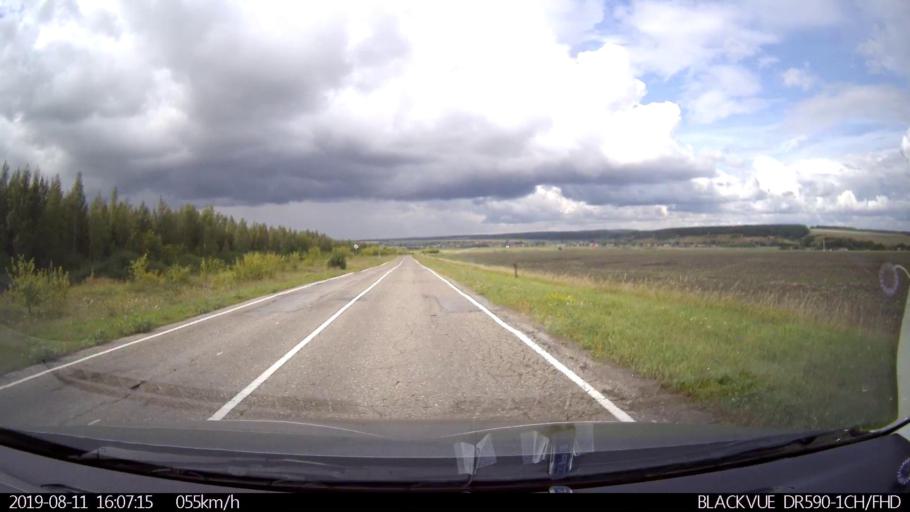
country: RU
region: Ulyanovsk
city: Ignatovka
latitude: 53.9748
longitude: 47.6515
